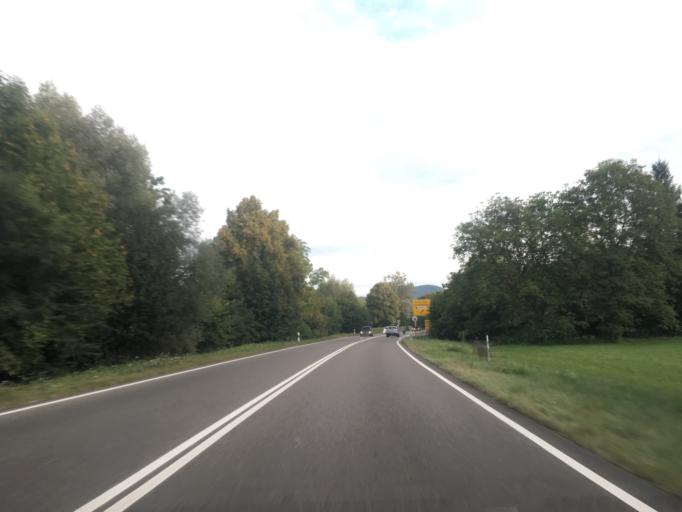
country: DE
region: Baden-Wuerttemberg
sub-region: Tuebingen Region
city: Riederich
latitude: 48.5448
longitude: 9.2673
